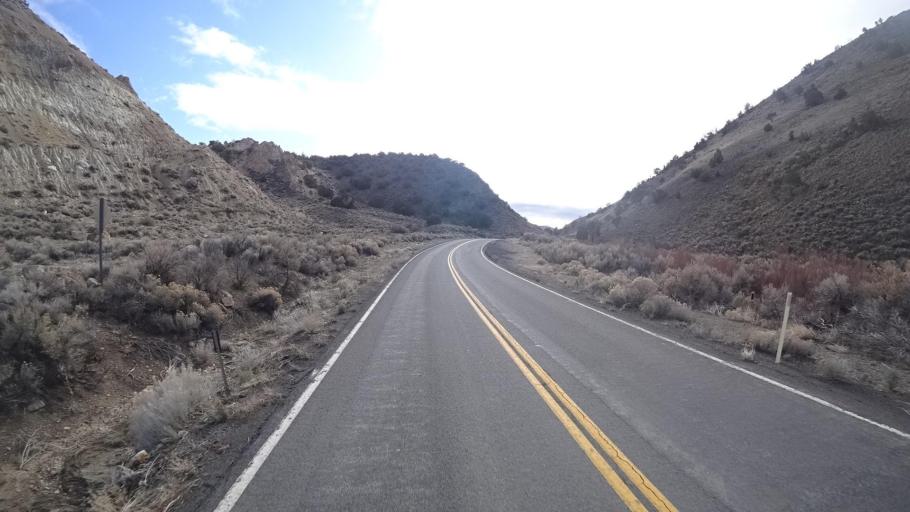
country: US
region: Nevada
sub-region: Washoe County
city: Cold Springs
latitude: 39.9041
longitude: -119.9914
